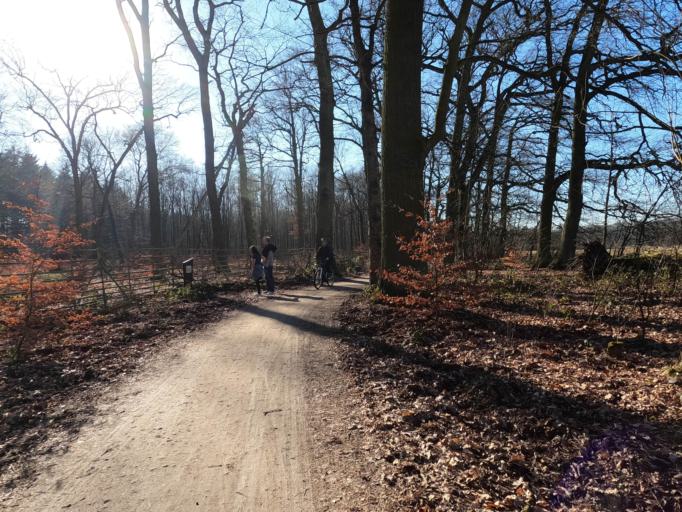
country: DE
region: Hesse
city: Kelsterbach
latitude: 50.0762
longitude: 8.5639
